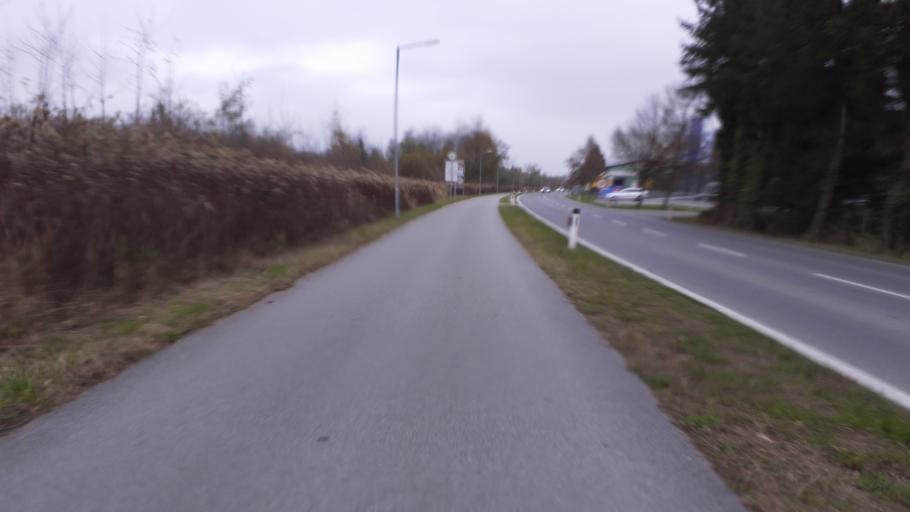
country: AT
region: Vorarlberg
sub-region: Politischer Bezirk Feldkirch
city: Nofels
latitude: 47.2677
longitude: 9.5908
